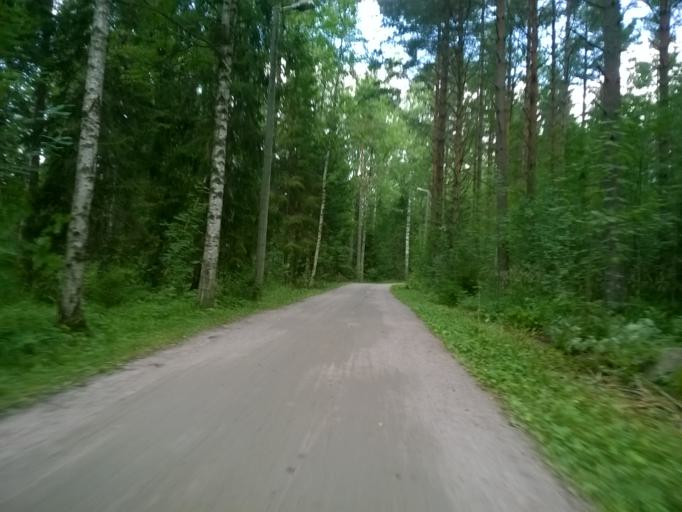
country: FI
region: Uusimaa
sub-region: Helsinki
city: Helsinki
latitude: 60.2607
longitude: 24.9097
